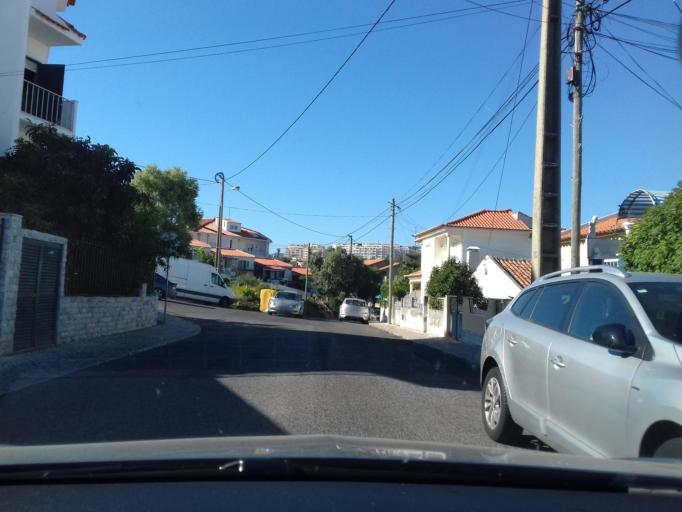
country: PT
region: Lisbon
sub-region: Cascais
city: Alcabideche
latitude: 38.7223
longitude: -9.4101
